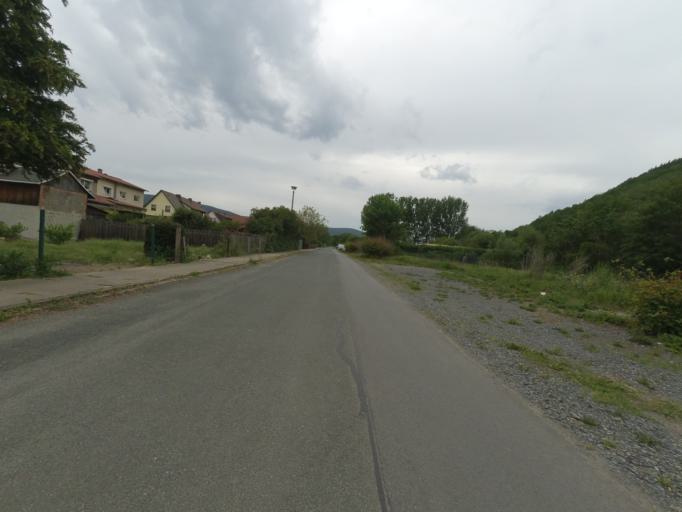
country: DE
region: Thuringia
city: Bad Blankenburg
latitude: 50.6867
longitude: 11.3100
